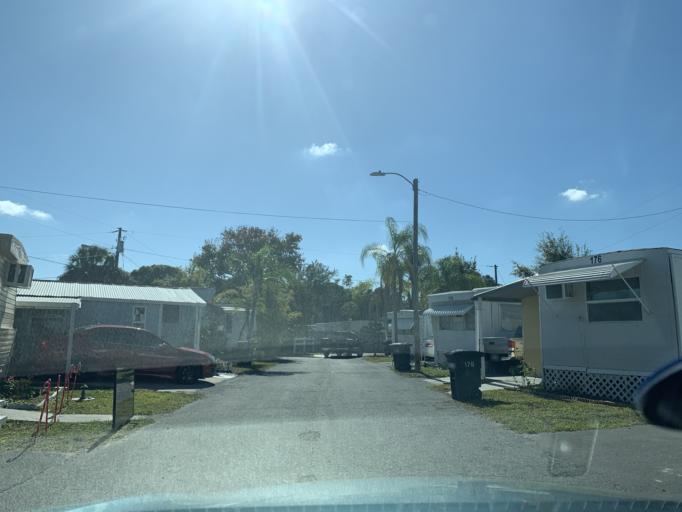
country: US
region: Florida
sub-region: Pinellas County
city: Kenneth City
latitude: 27.8105
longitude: -82.7437
